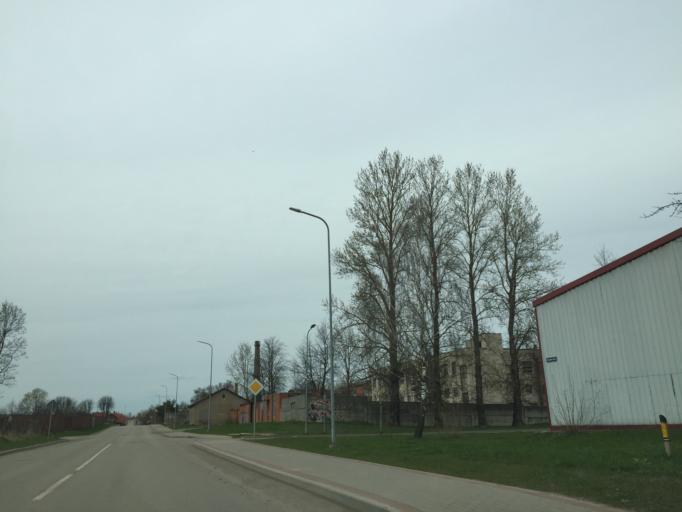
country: LV
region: Ludzas Rajons
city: Ludza
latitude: 56.5378
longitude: 27.7052
